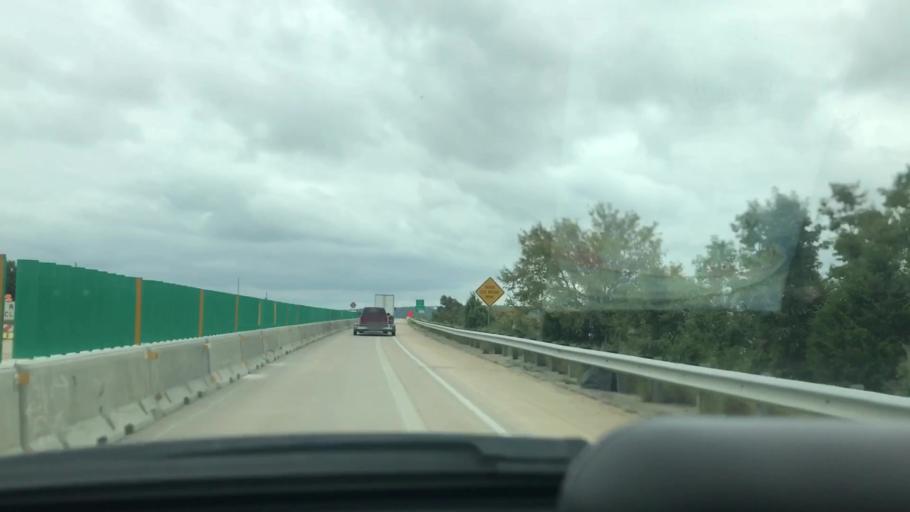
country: US
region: Oklahoma
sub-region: McIntosh County
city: Eufaula
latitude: 35.2209
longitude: -95.6076
